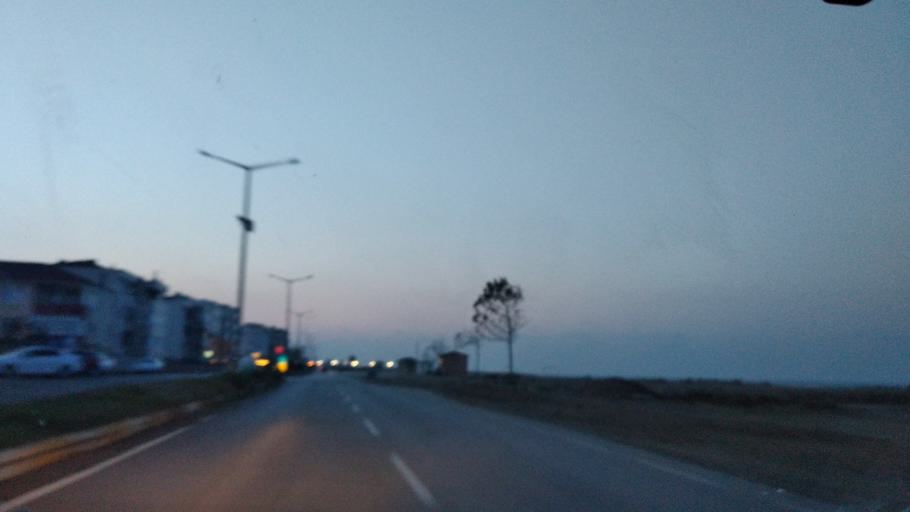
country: TR
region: Sakarya
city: Karasu
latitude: 41.1004
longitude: 30.7193
